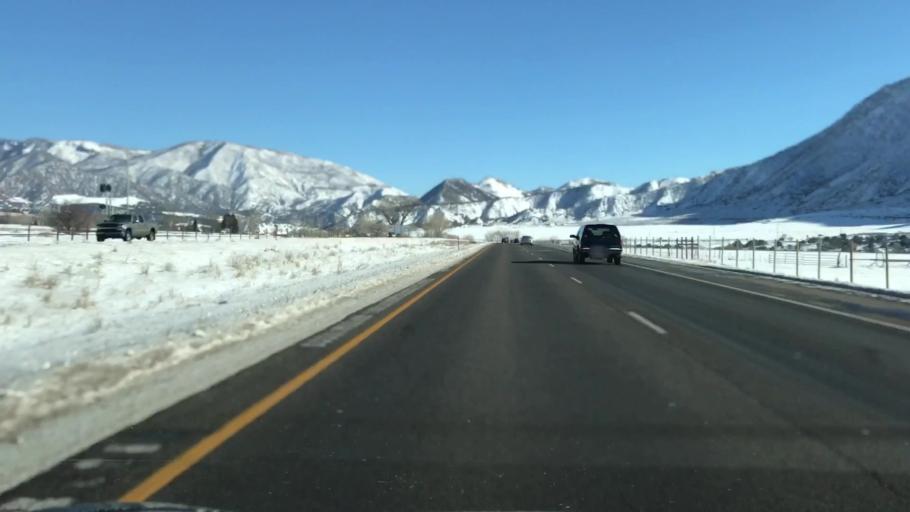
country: US
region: Colorado
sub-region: Garfield County
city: New Castle
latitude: 39.5658
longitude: -107.5007
